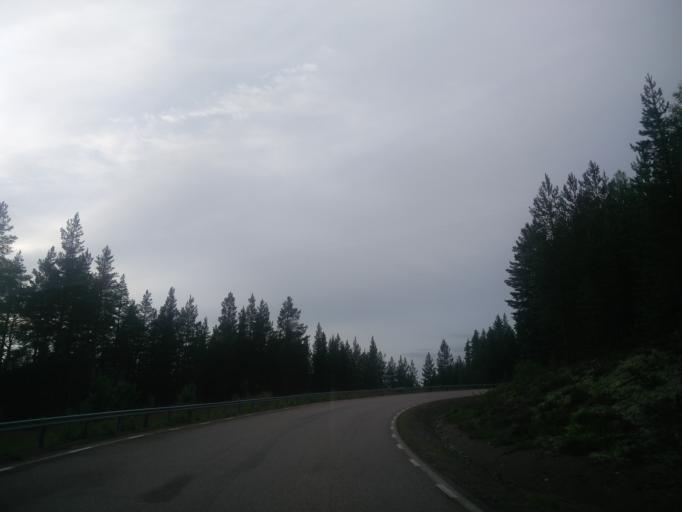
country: NO
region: Hedmark
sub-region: Trysil
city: Innbygda
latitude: 61.7964
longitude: 12.9204
